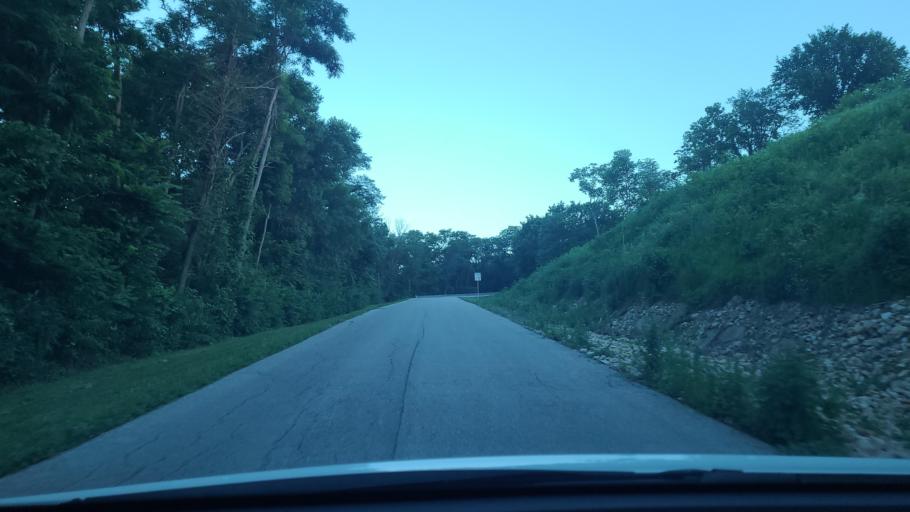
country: US
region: Kansas
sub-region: Douglas County
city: Lawrence
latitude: 38.8839
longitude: -95.2467
